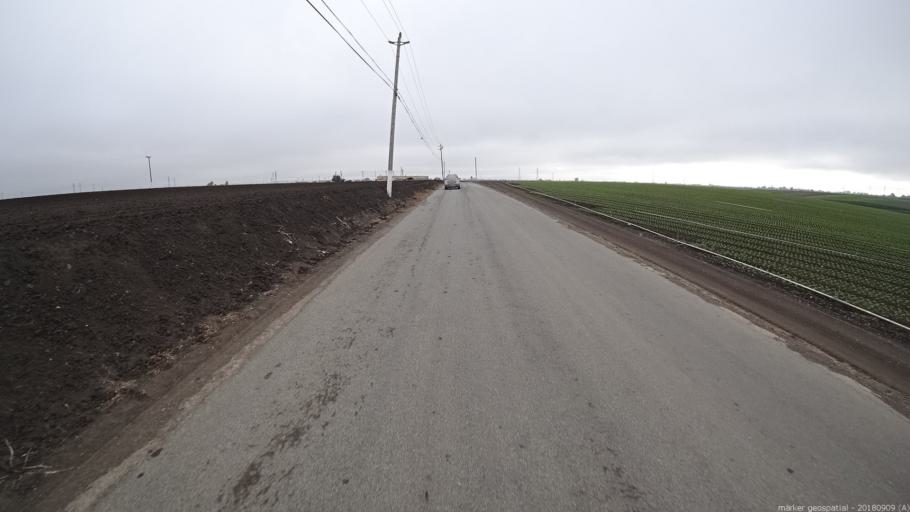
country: US
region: California
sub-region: Monterey County
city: Boronda
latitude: 36.7065
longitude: -121.7032
